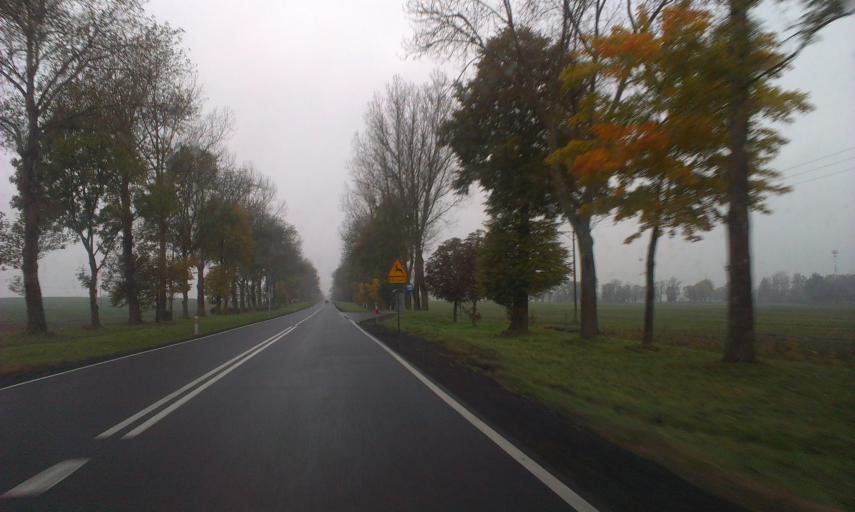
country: PL
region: West Pomeranian Voivodeship
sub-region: Powiat koszalinski
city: Sianow
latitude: 54.1406
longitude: 16.2679
